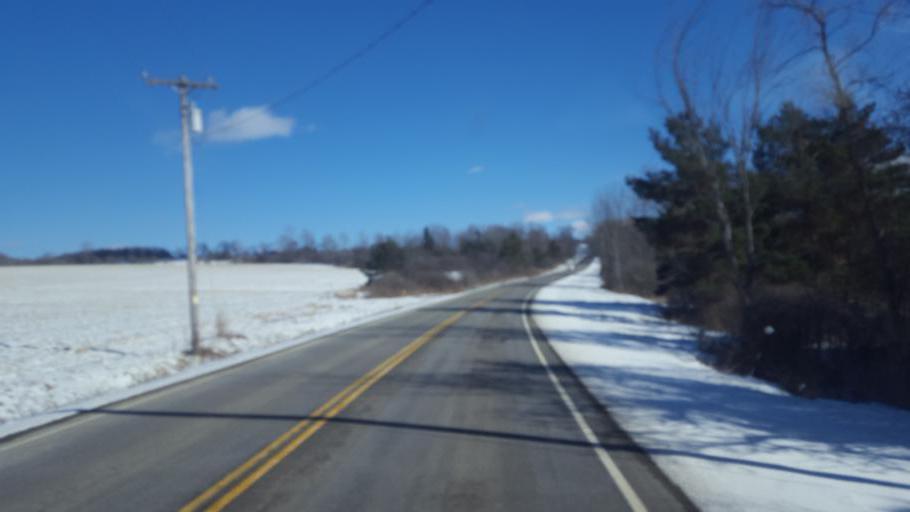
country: US
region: New York
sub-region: Allegany County
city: Friendship
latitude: 42.2010
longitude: -78.1089
